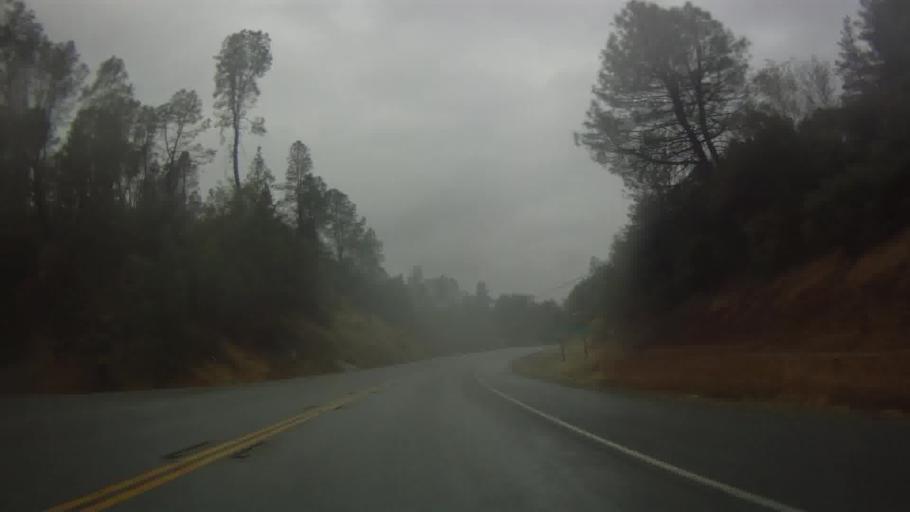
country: US
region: California
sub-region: Shasta County
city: Shasta
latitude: 40.5917
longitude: -122.4832
